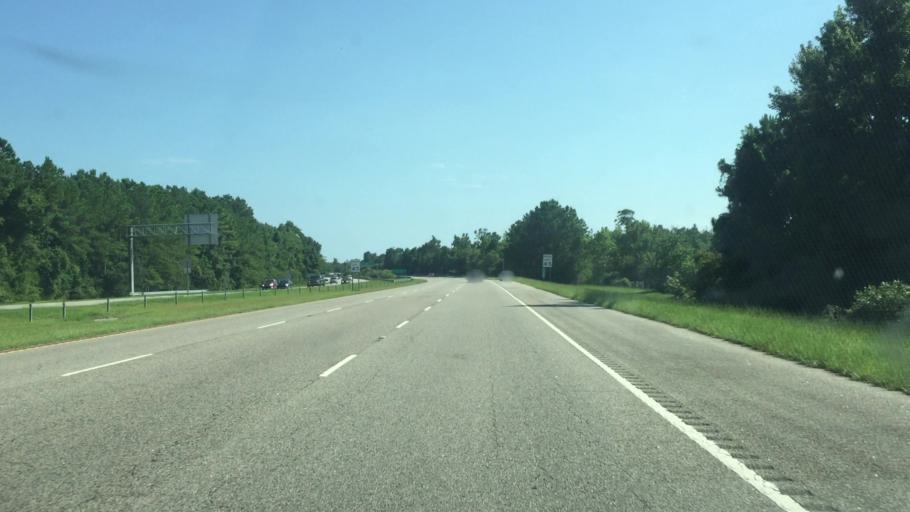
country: US
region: South Carolina
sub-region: Horry County
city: North Myrtle Beach
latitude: 33.8009
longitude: -78.7794
